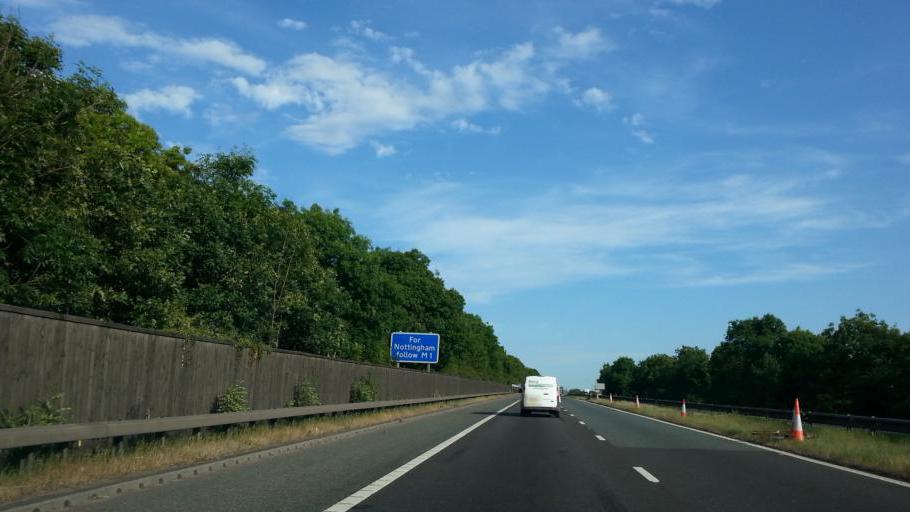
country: GB
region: England
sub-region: Doncaster
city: Doncaster
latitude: 53.4880
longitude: -1.1576
